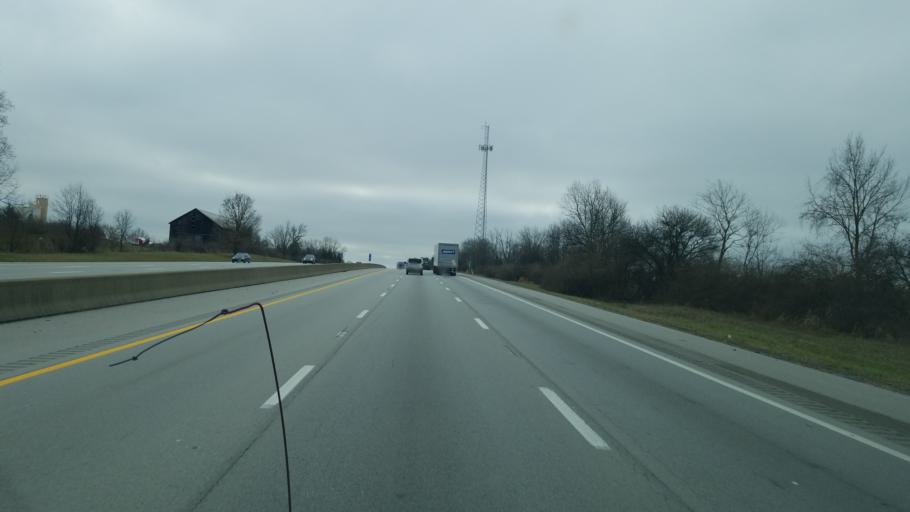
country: US
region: Kentucky
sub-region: Scott County
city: Georgetown
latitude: 38.2059
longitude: -84.5303
